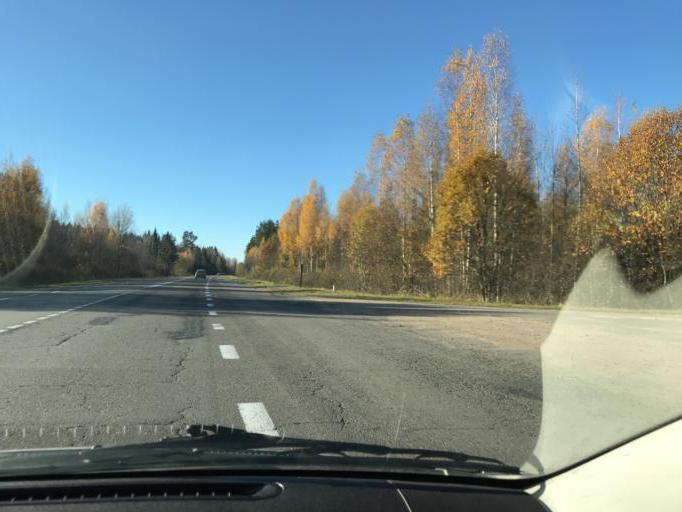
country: BY
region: Vitebsk
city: Syanno
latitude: 55.0426
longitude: 29.5124
